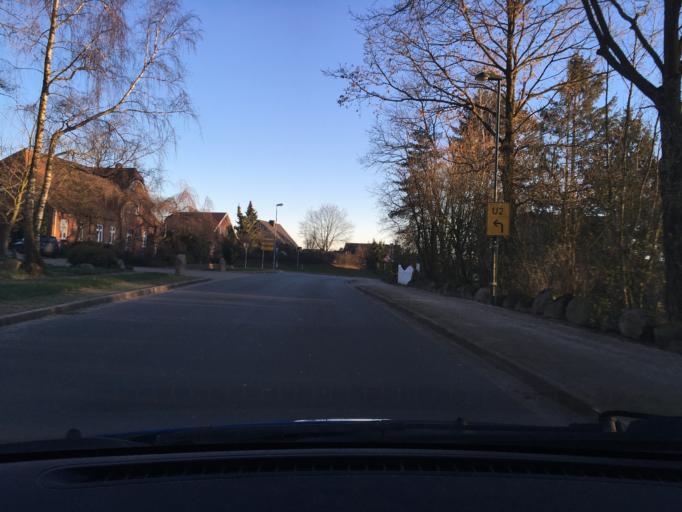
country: DE
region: Lower Saxony
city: Dahlem
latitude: 53.1876
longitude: 10.7531
